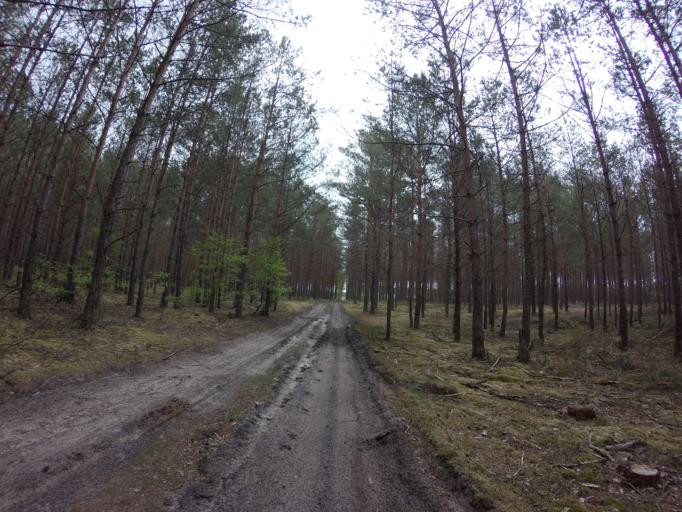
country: PL
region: West Pomeranian Voivodeship
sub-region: Powiat drawski
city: Kalisz Pomorski
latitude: 53.1883
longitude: 15.9919
